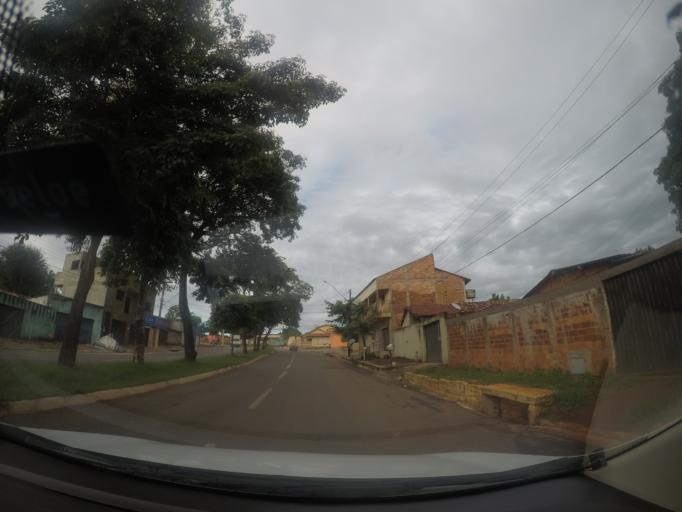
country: BR
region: Goias
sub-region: Goiania
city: Goiania
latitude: -16.6095
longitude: -49.3414
